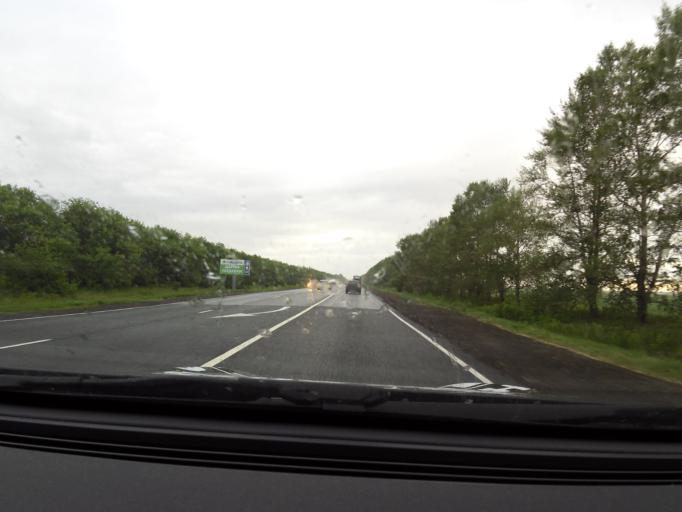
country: RU
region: Chuvashia
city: Yantikovo
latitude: 55.8026
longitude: 47.8942
